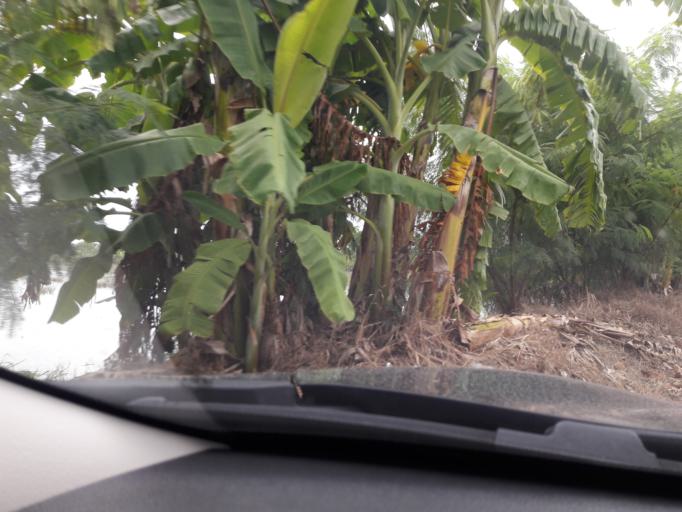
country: TH
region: Ratchaburi
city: Damnoen Saduak
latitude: 13.5980
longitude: 99.9537
